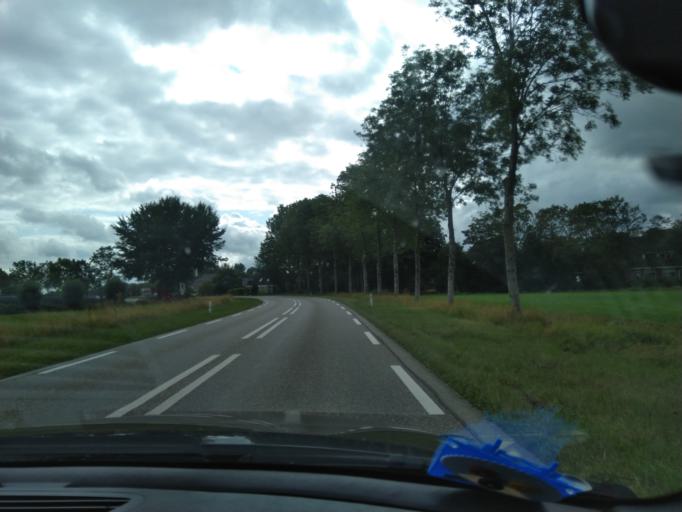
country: NL
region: Groningen
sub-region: Gemeente Zuidhorn
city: Grijpskerk
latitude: 53.2625
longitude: 6.3178
